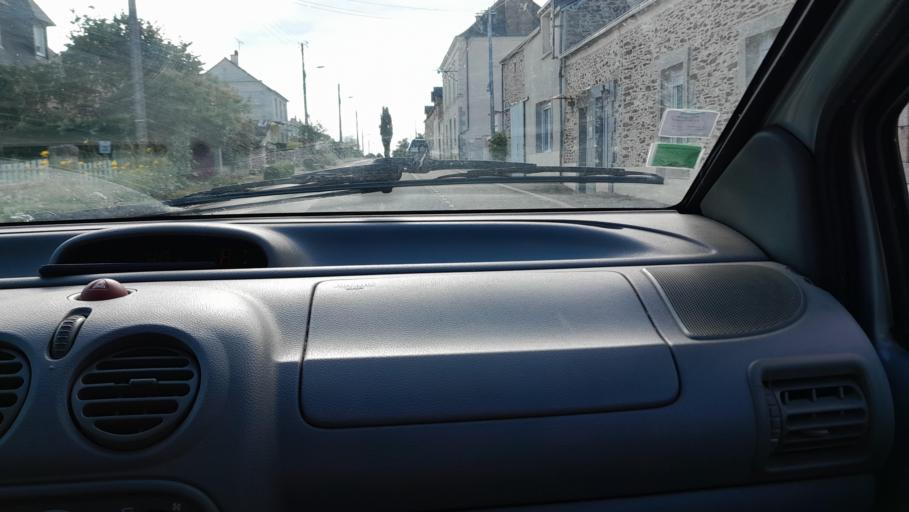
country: FR
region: Pays de la Loire
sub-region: Departement de la Mayenne
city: Loiron
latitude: 48.0041
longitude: -0.9641
